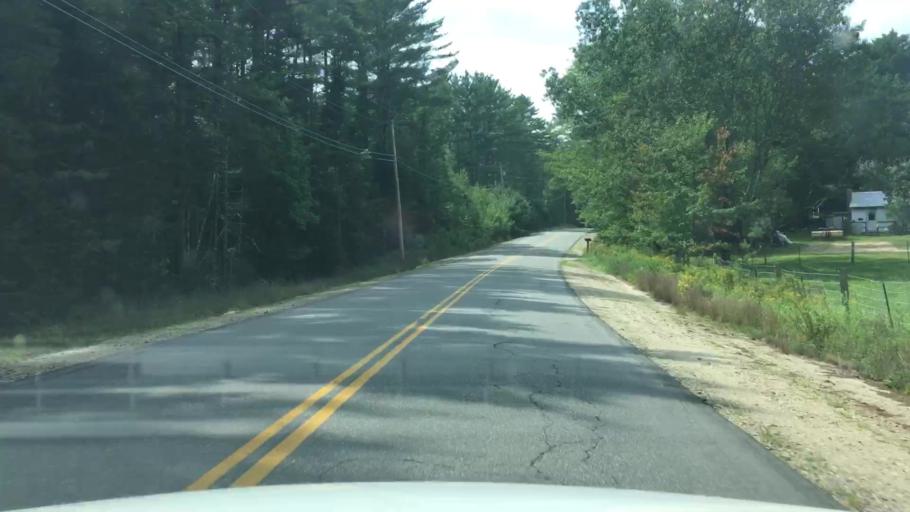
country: US
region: Maine
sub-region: Oxford County
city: Rumford
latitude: 44.5311
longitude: -70.6558
